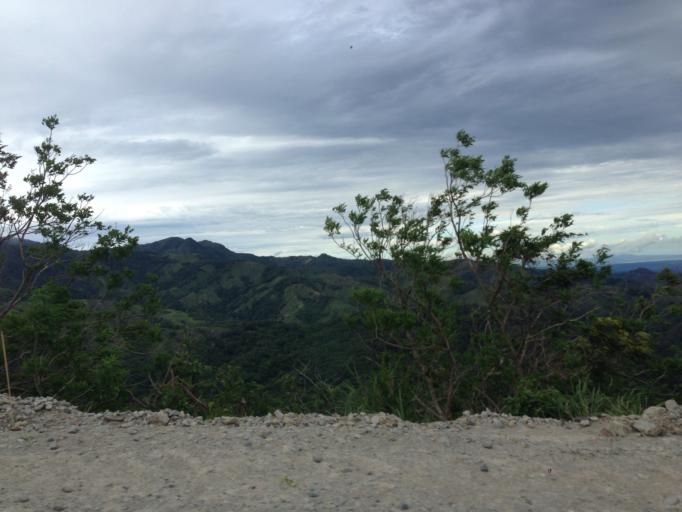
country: CR
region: Guanacaste
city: Juntas
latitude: 10.2630
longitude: -84.8354
